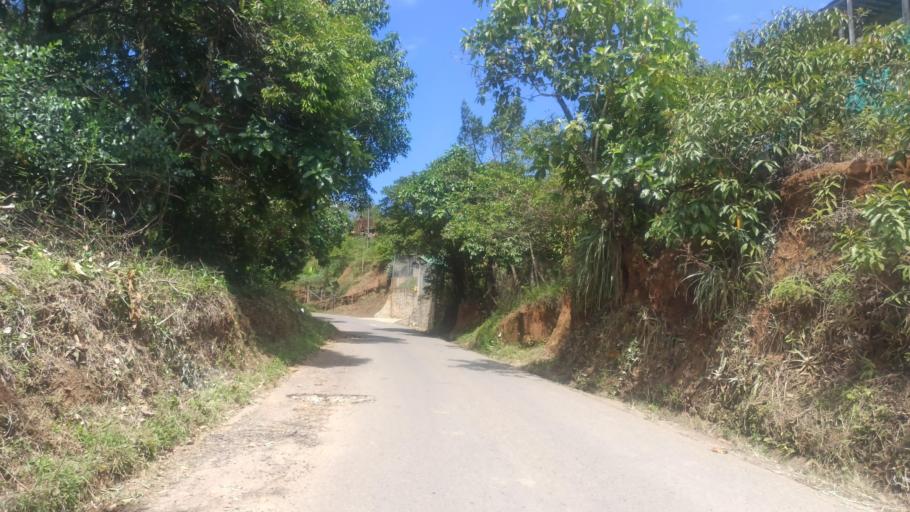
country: CO
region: Valle del Cauca
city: Jamundi
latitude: 3.1924
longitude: -76.6277
